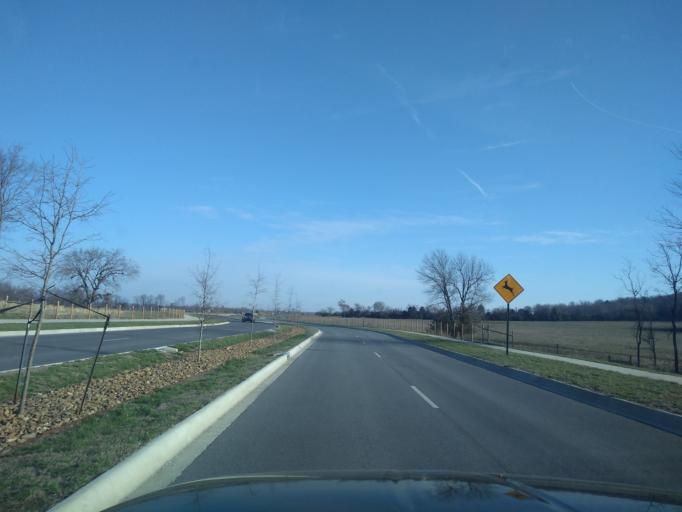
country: US
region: Arkansas
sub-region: Washington County
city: Farmington
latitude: 36.0530
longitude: -94.2199
